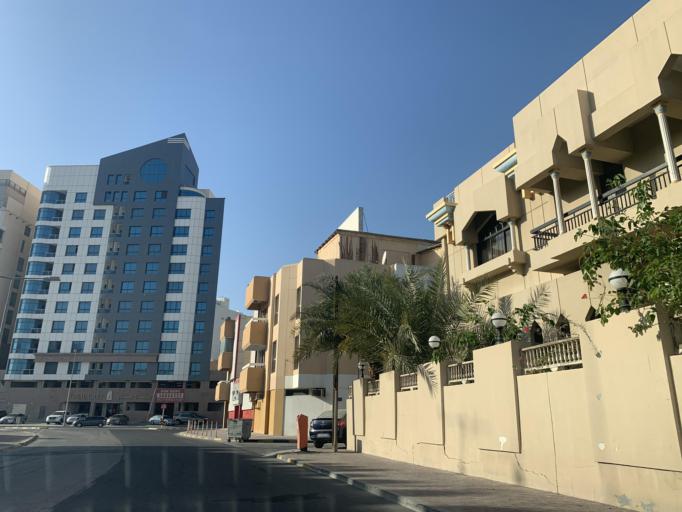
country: BH
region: Manama
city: Manama
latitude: 26.2027
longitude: 50.5854
